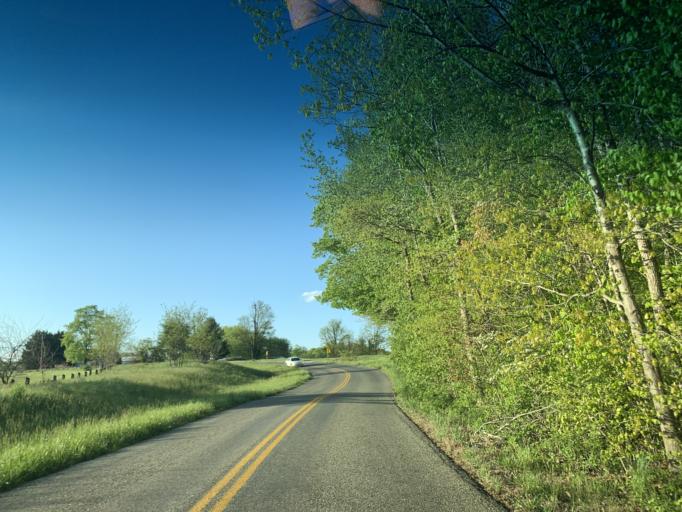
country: US
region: Maryland
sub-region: Harford County
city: Aberdeen
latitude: 39.5485
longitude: -76.1804
